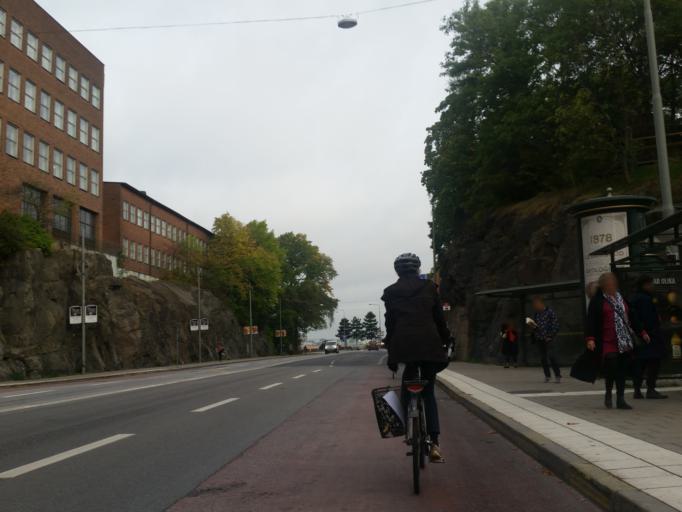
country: SE
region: Stockholm
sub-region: Stockholms Kommun
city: OEstermalm
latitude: 59.3162
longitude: 18.0836
